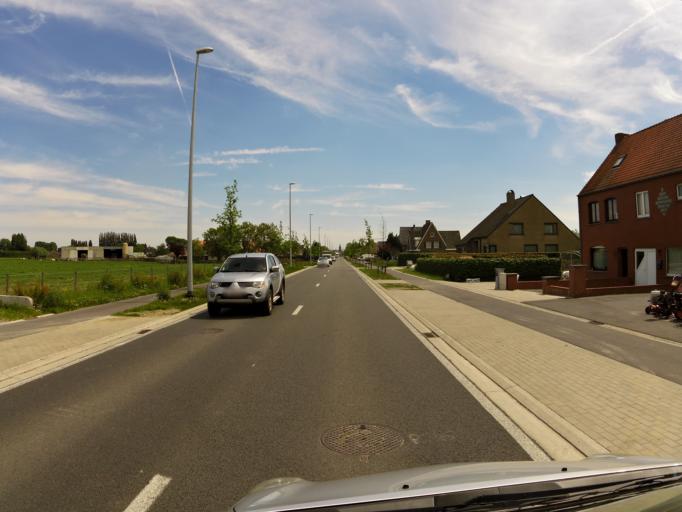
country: BE
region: Flanders
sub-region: Provincie West-Vlaanderen
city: Torhout
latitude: 51.0741
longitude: 3.0745
